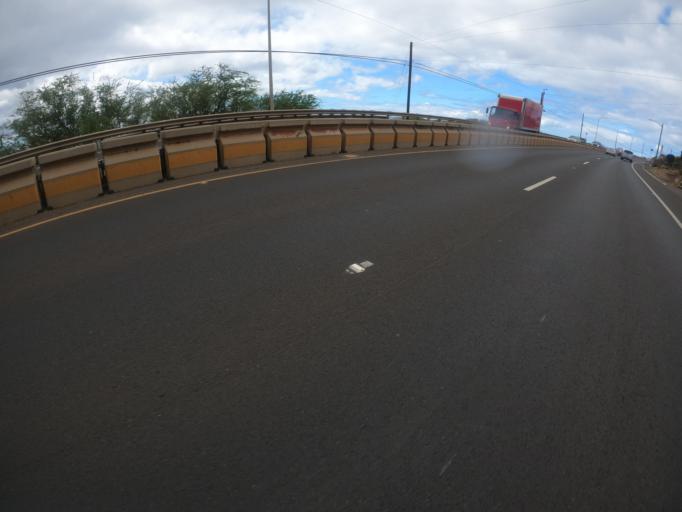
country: US
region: Hawaii
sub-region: Honolulu County
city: Nanakuli
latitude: 21.3984
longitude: -158.1705
